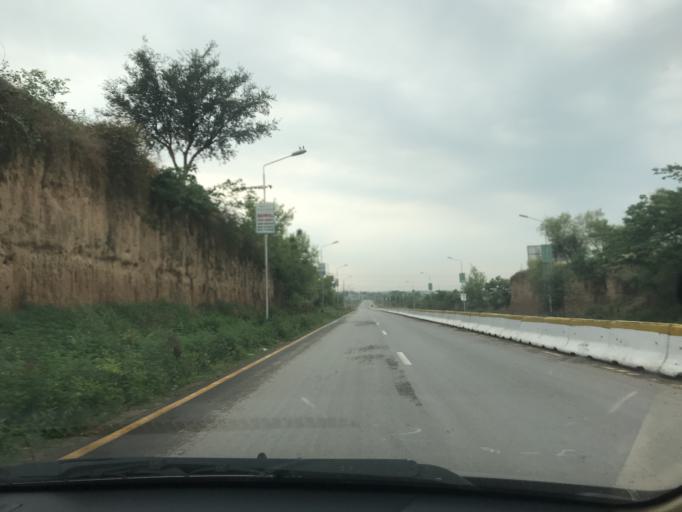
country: PK
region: Islamabad
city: Islamabad
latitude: 33.6998
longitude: 73.1848
